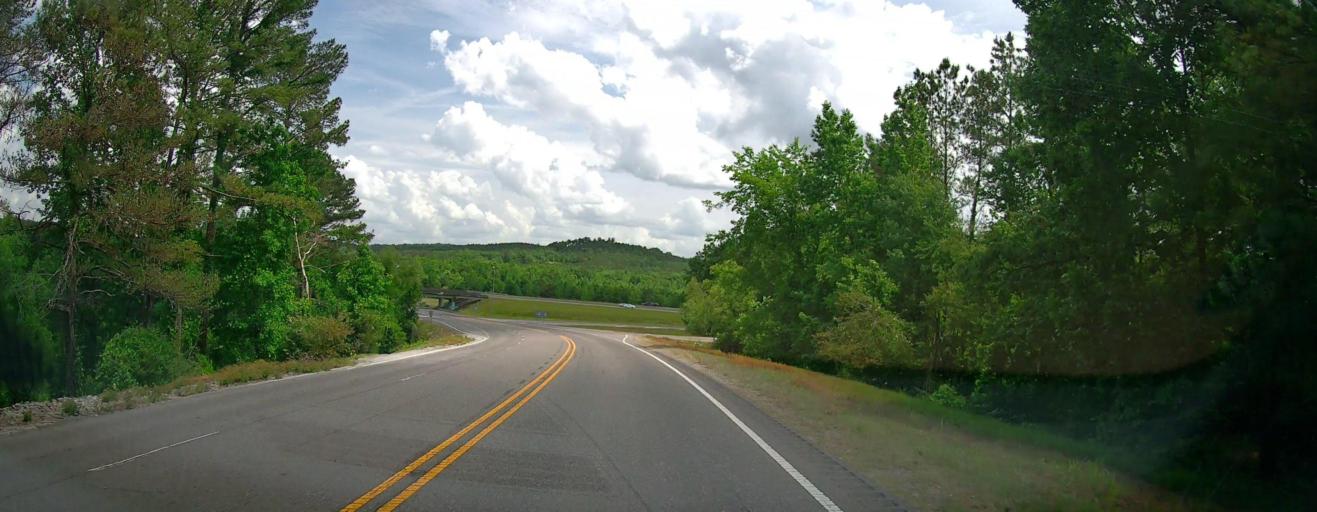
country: US
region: Alabama
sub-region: Marion County
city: Hamilton
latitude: 34.0750
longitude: -87.9771
